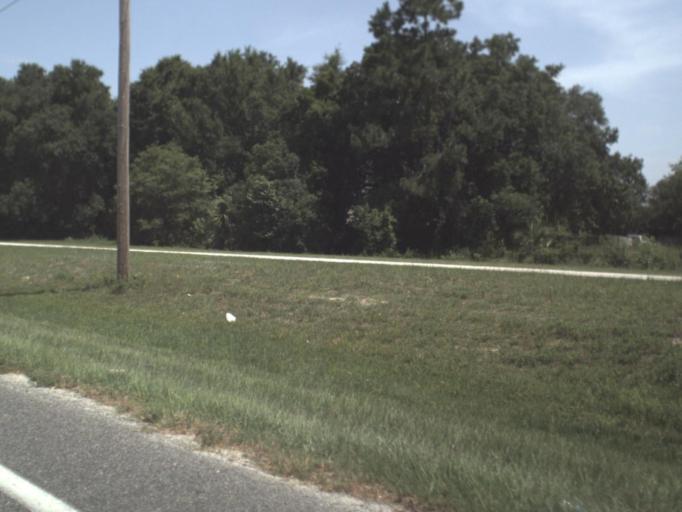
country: US
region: Florida
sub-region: Dixie County
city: Cross City
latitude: 29.6260
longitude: -83.1105
